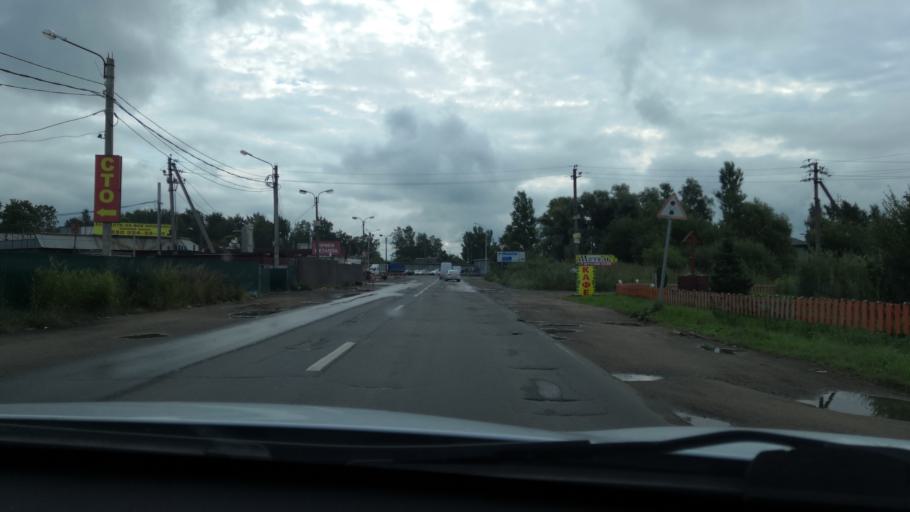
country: RU
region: St.-Petersburg
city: Kolpino
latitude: 59.7042
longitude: 30.5759
